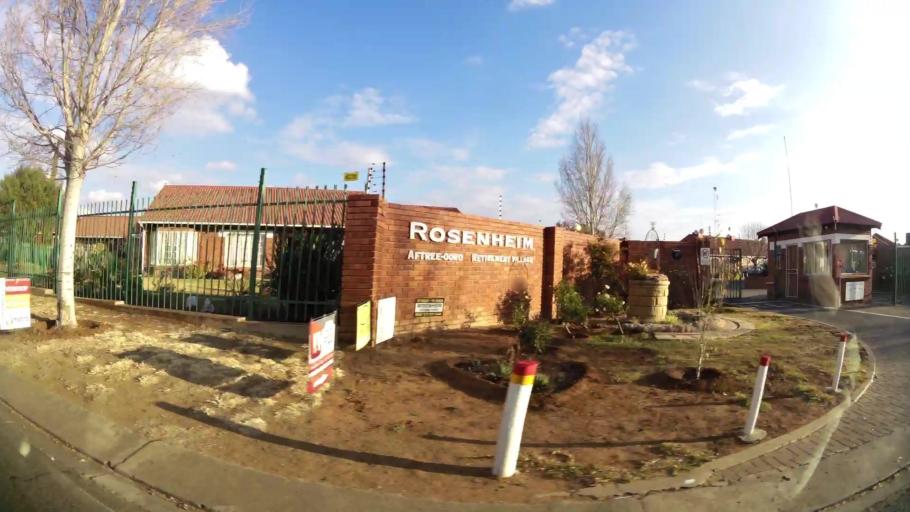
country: ZA
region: Orange Free State
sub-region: Mangaung Metropolitan Municipality
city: Bloemfontein
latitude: -29.1484
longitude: 26.1888
